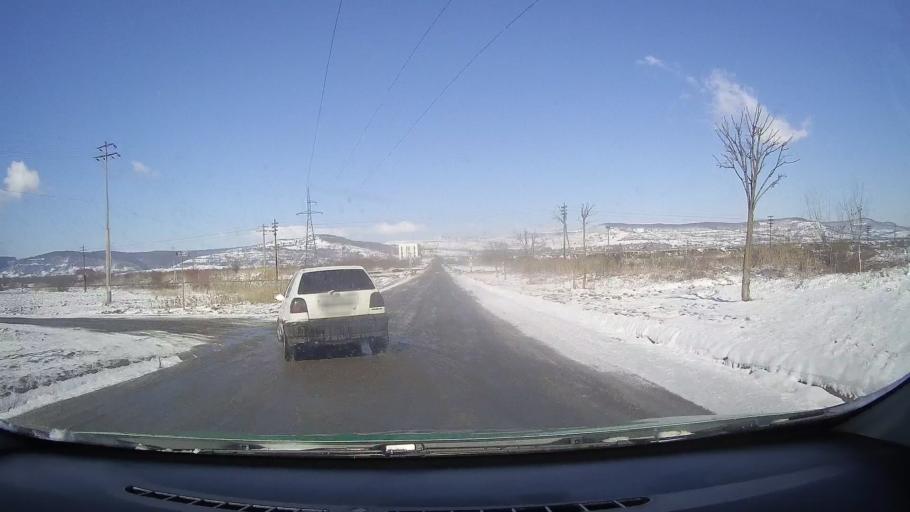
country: RO
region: Sibiu
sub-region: Comuna Avrig
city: Avrig
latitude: 45.7394
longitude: 24.3925
